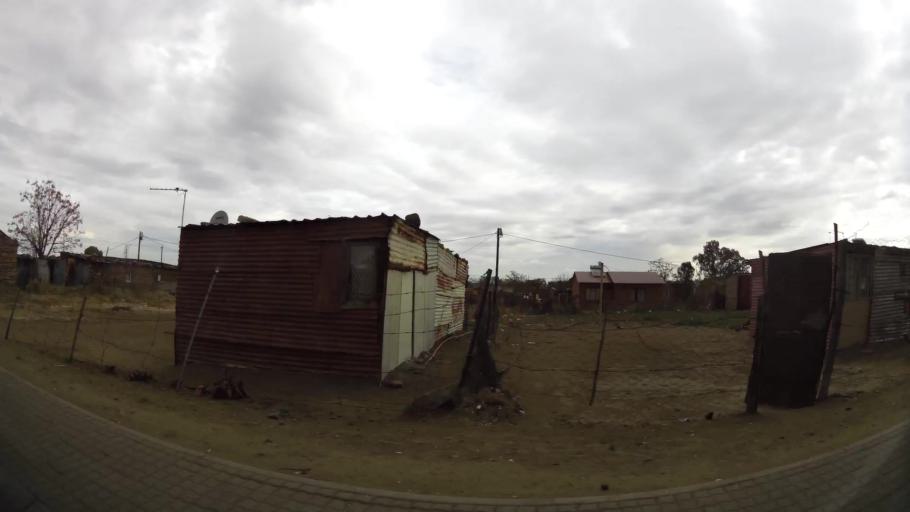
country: ZA
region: Orange Free State
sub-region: Fezile Dabi District Municipality
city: Kroonstad
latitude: -27.6486
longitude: 27.2200
